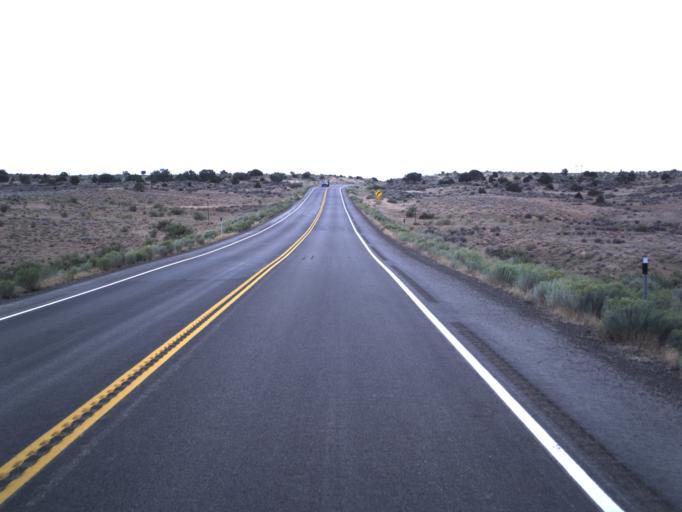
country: US
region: Utah
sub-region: Uintah County
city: Naples
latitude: 40.1960
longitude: -109.3341
